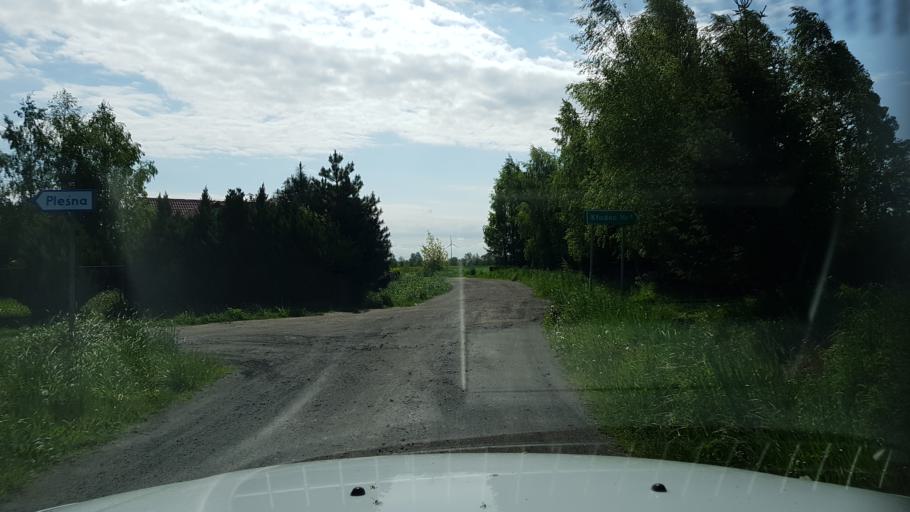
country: PL
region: West Pomeranian Voivodeship
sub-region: Powiat kolobrzeski
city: Ustronie Morskie
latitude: 54.2173
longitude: 15.8330
